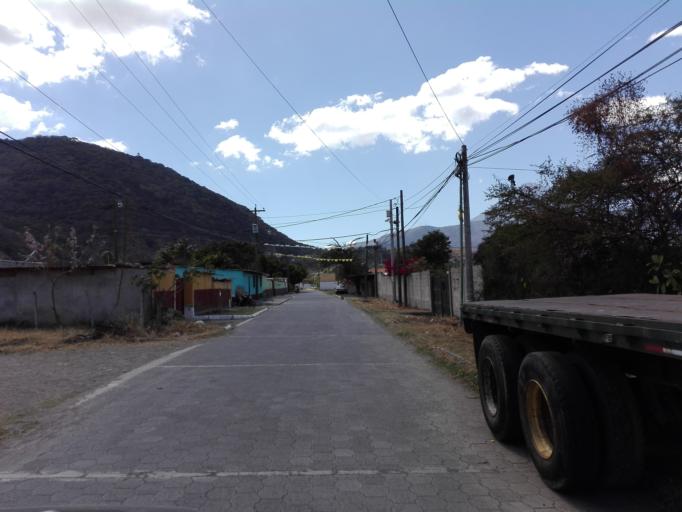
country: GT
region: Guatemala
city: Amatitlan
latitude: 14.4760
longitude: -90.5997
